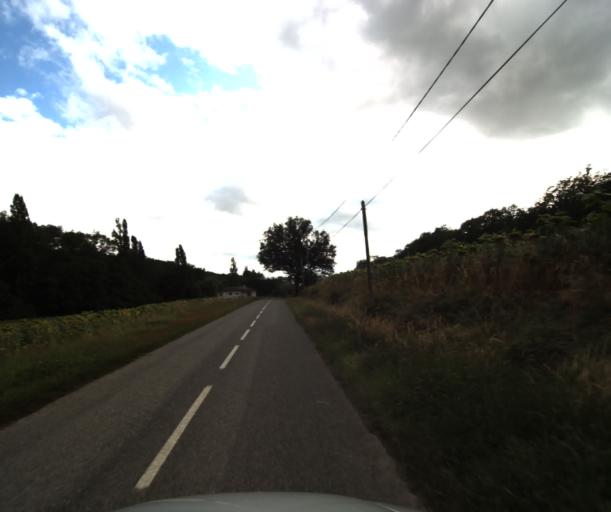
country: FR
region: Midi-Pyrenees
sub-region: Departement de la Haute-Garonne
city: Eaunes
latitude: 43.4182
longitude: 1.3423
